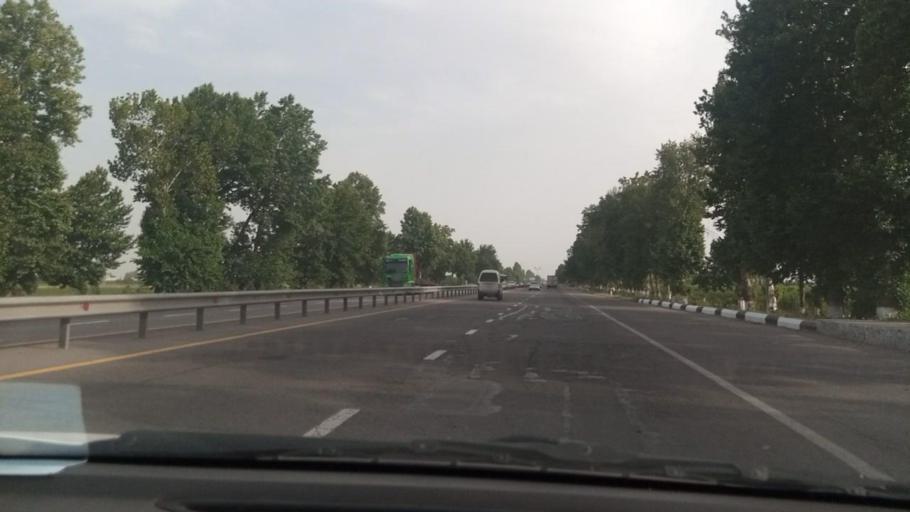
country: UZ
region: Toshkent Shahri
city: Bektemir
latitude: 41.2232
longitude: 69.4024
